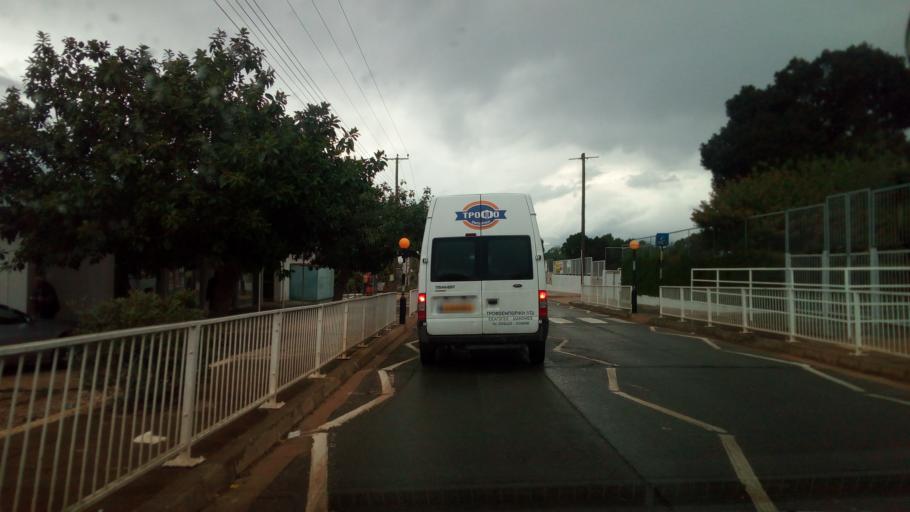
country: CY
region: Ammochostos
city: Liopetri
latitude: 35.0018
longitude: 33.8928
